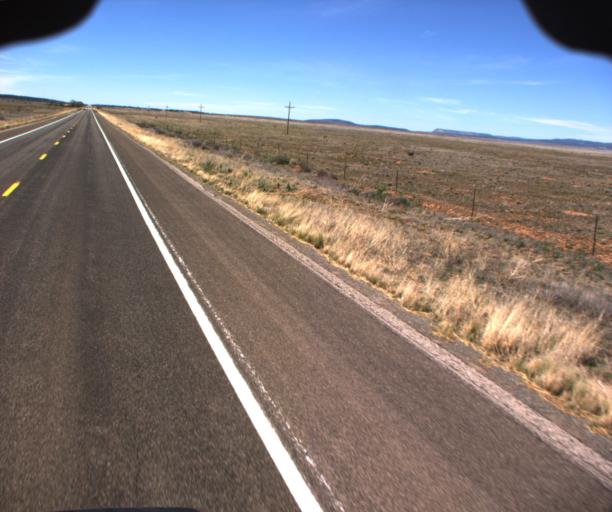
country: US
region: Arizona
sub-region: Mohave County
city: Peach Springs
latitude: 35.4701
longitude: -113.1247
